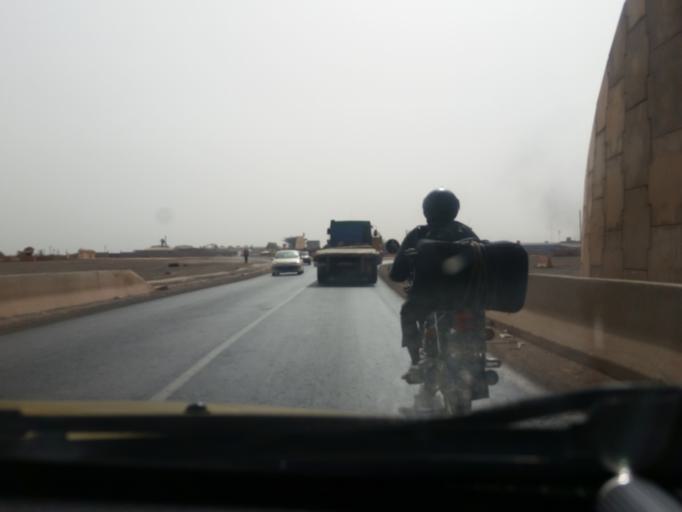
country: SN
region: Thies
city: Pout
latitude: 14.7319
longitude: -17.1594
